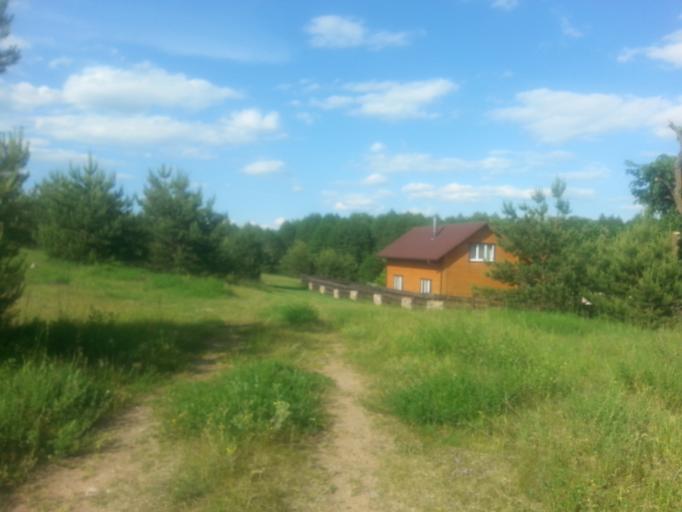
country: BY
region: Minsk
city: Narach
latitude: 54.9771
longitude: 26.6066
